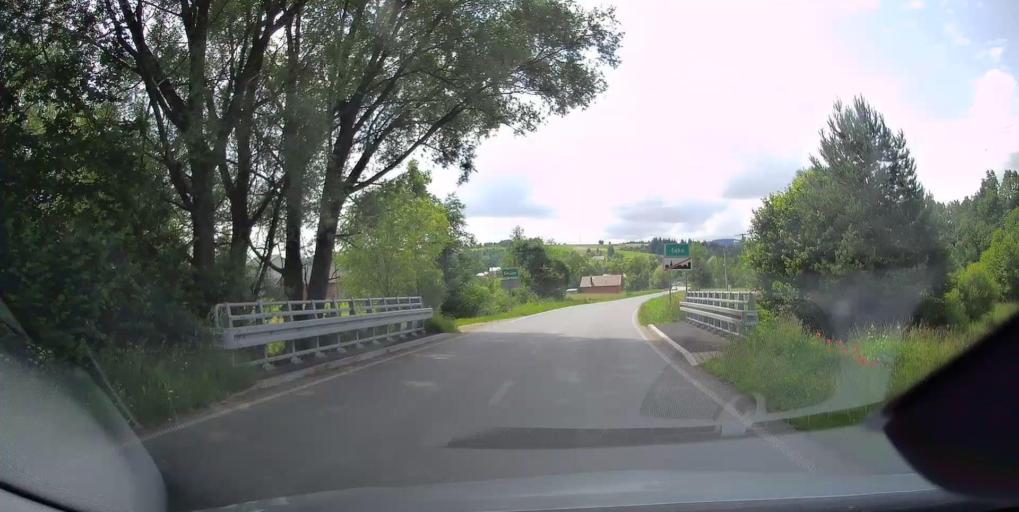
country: PL
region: Lesser Poland Voivodeship
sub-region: Powiat nowosadecki
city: Korzenna
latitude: 49.6775
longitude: 20.7774
